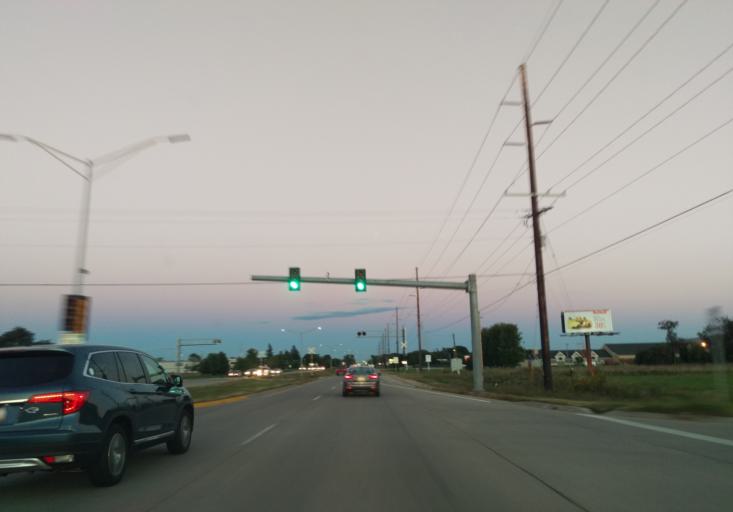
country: US
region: Wisconsin
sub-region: Rock County
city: Janesville
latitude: 42.7248
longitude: -89.0134
